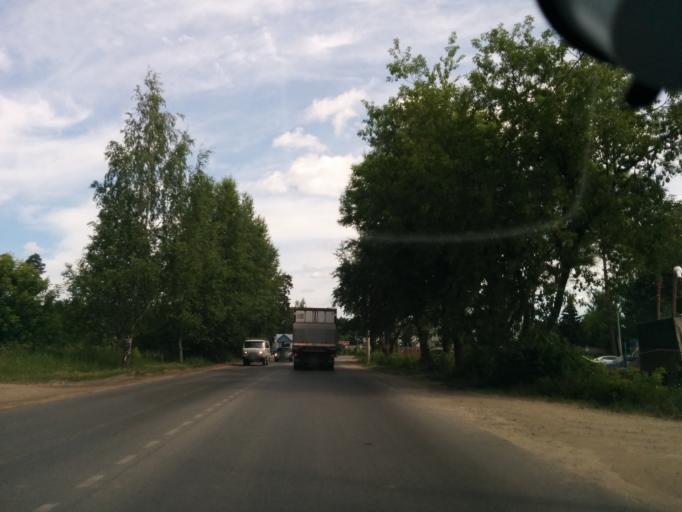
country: RU
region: Perm
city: Overyata
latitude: 58.0195
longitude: 55.9732
